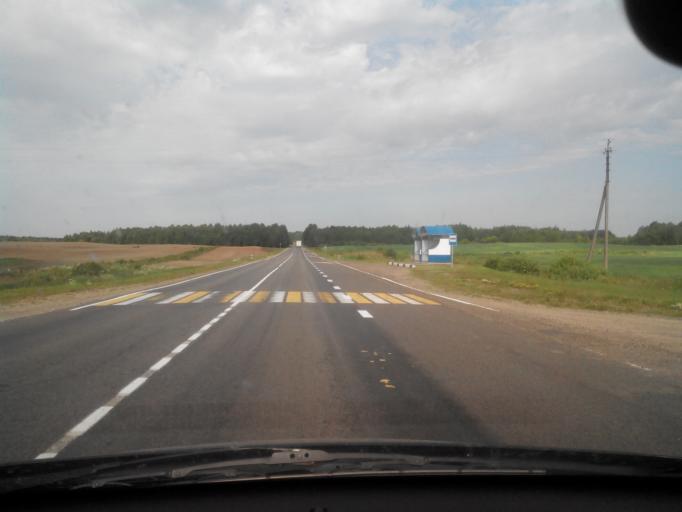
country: BY
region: Minsk
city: Myadzyel
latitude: 55.0626
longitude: 27.1633
